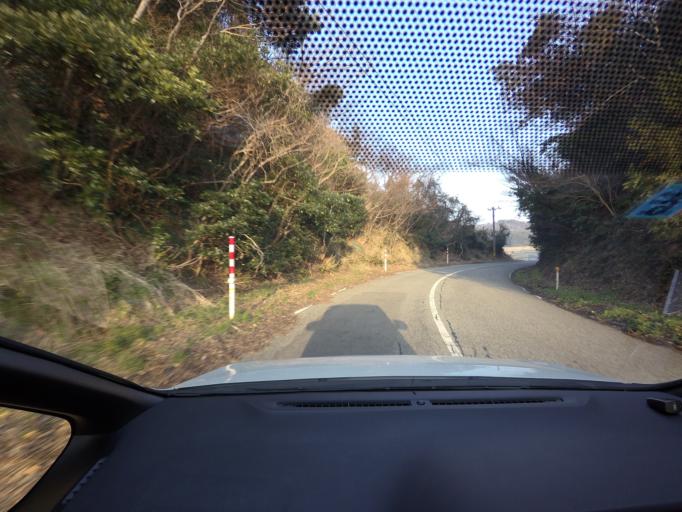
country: JP
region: Ishikawa
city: Nanao
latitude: 37.1415
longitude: 137.0090
